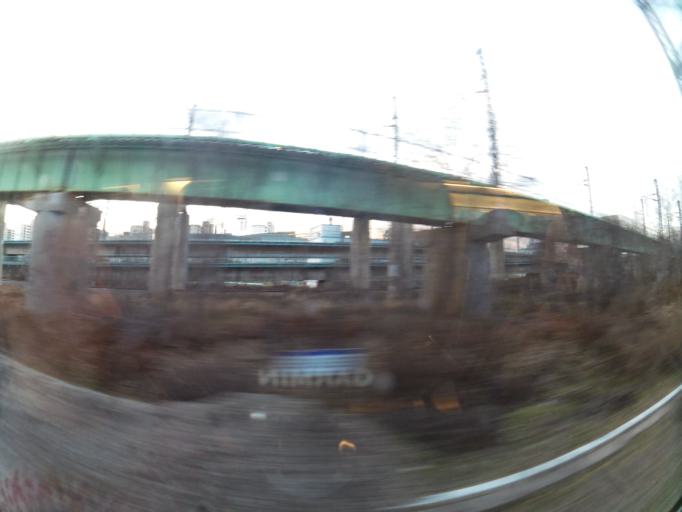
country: KR
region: Gyeonggi-do
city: Kwangmyong
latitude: 37.4971
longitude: 126.8793
